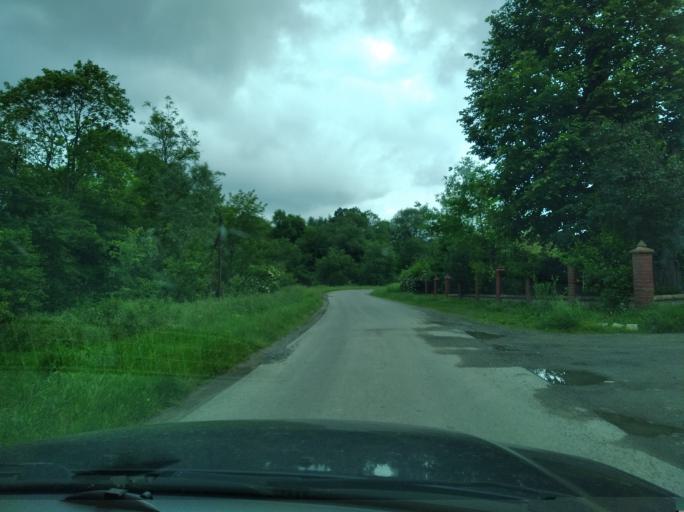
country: PL
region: Subcarpathian Voivodeship
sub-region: Powiat przemyski
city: Nienadowa
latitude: 49.8484
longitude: 22.4110
